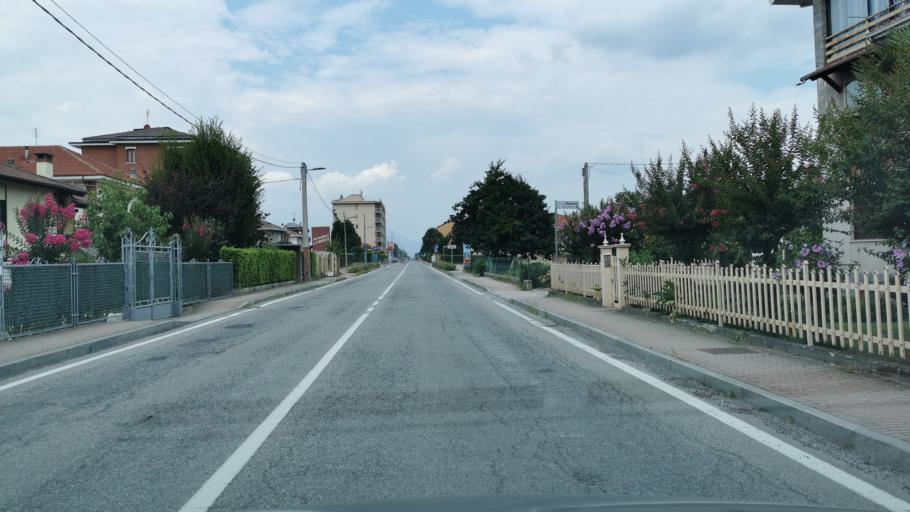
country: IT
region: Piedmont
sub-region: Provincia di Torino
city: Cavour
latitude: 44.7896
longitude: 7.3754
